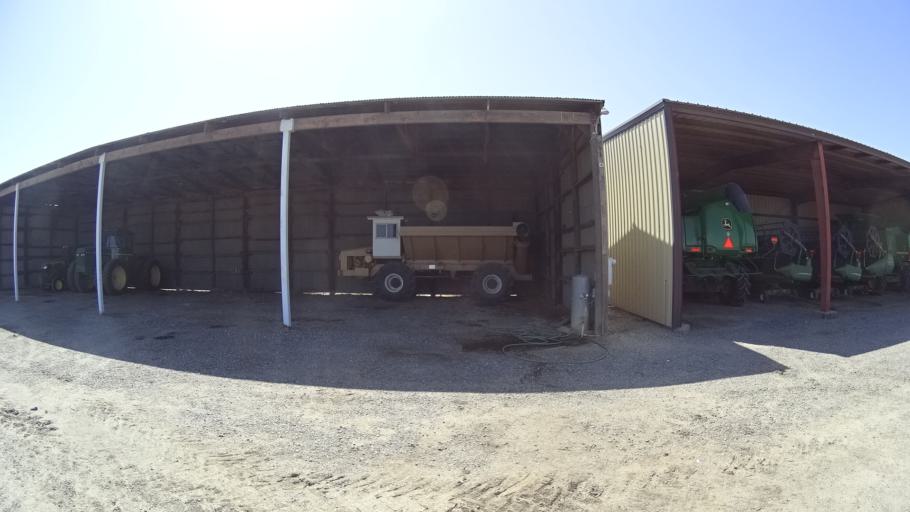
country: US
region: California
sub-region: Glenn County
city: Willows
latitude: 39.4211
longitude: -122.0465
